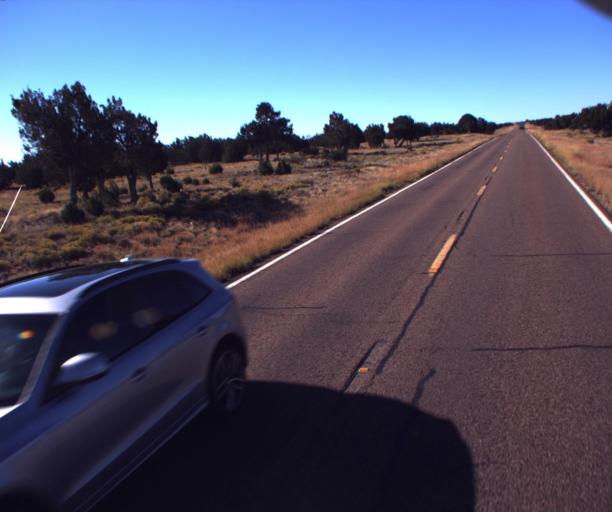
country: US
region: Arizona
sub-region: Navajo County
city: Heber-Overgaard
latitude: 34.4810
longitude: -110.4641
